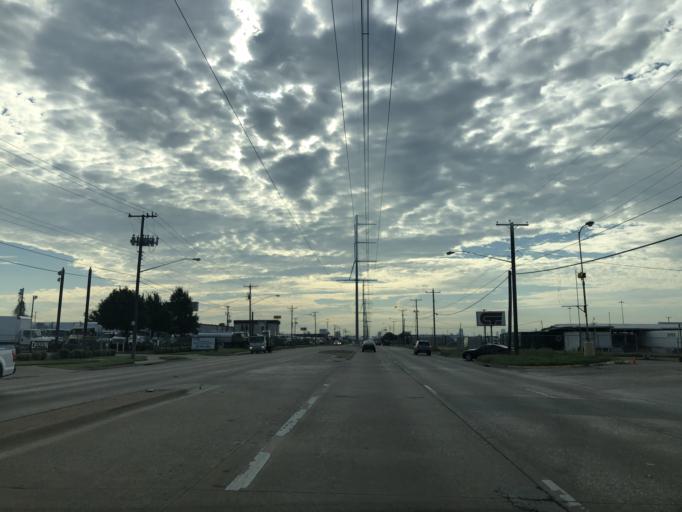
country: US
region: Texas
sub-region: Dallas County
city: Irving
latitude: 32.8081
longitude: -96.8952
